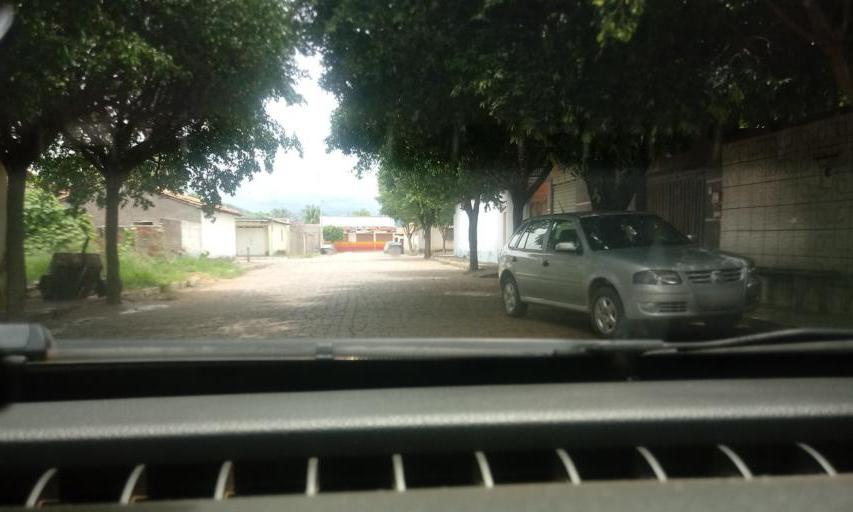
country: BR
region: Bahia
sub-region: Riacho De Santana
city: Riacho de Santana
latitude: -13.9092
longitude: -42.8438
